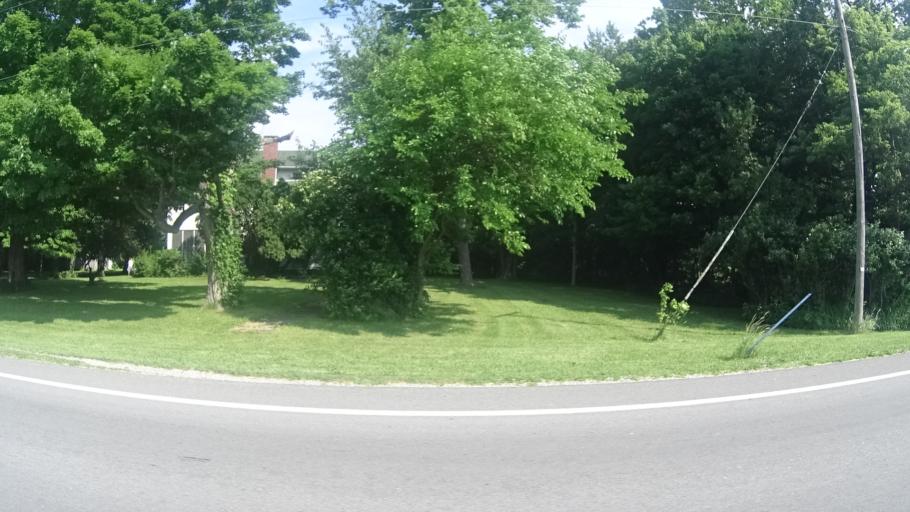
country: US
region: Ohio
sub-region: Huron County
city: Bellevue
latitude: 41.2911
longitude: -82.7734
